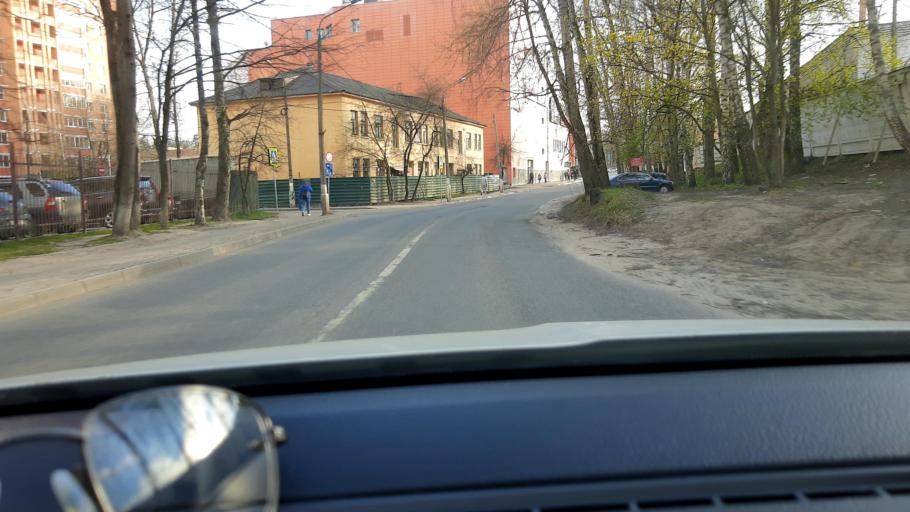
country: RU
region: Moskovskaya
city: Krasnogorsk
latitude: 55.8307
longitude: 37.3092
